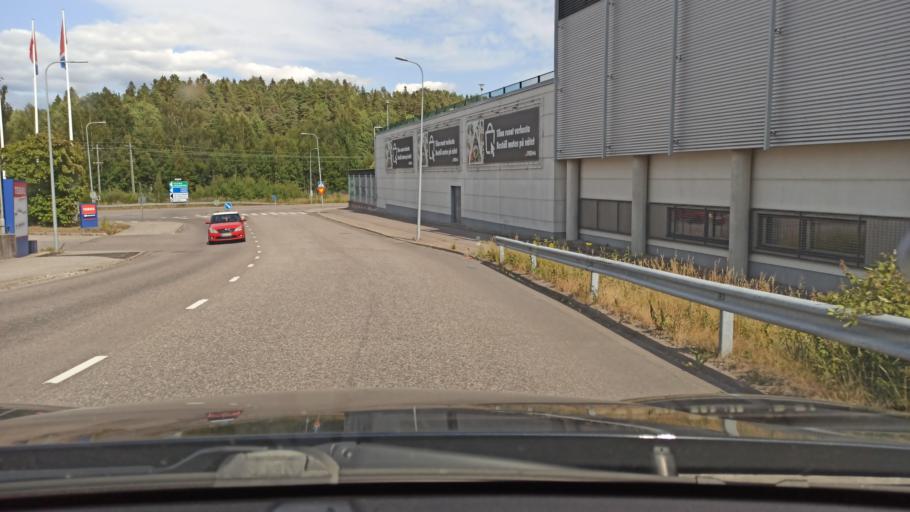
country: FI
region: Uusimaa
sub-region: Helsinki
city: Kirkkonummi
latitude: 60.1182
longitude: 24.4445
